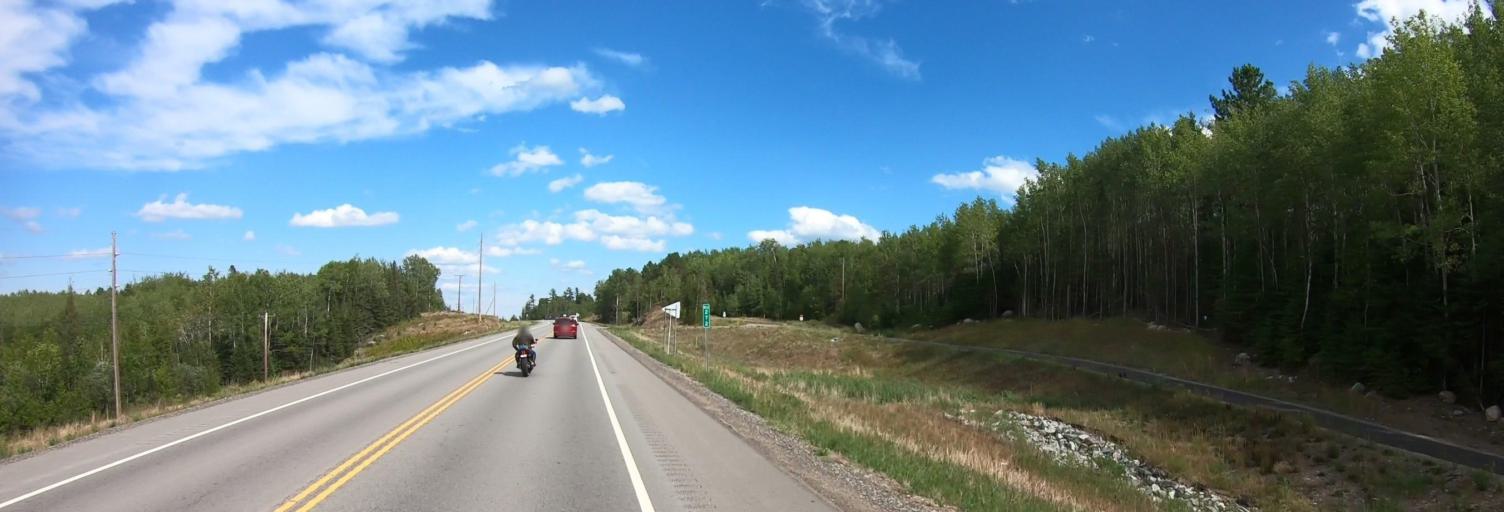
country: US
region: Minnesota
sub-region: Saint Louis County
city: Babbitt
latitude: 47.8486
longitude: -92.1109
